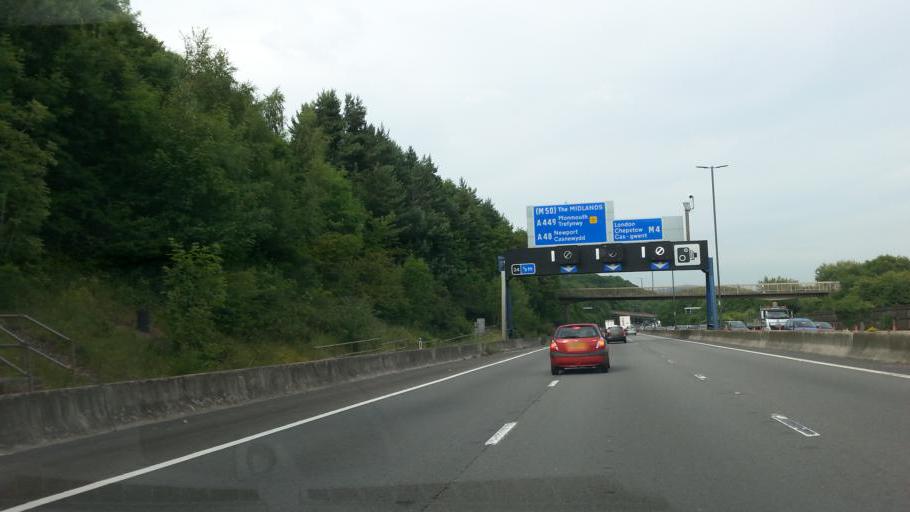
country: GB
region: Wales
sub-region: Newport
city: Caerleon
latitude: 51.5966
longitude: -2.9456
